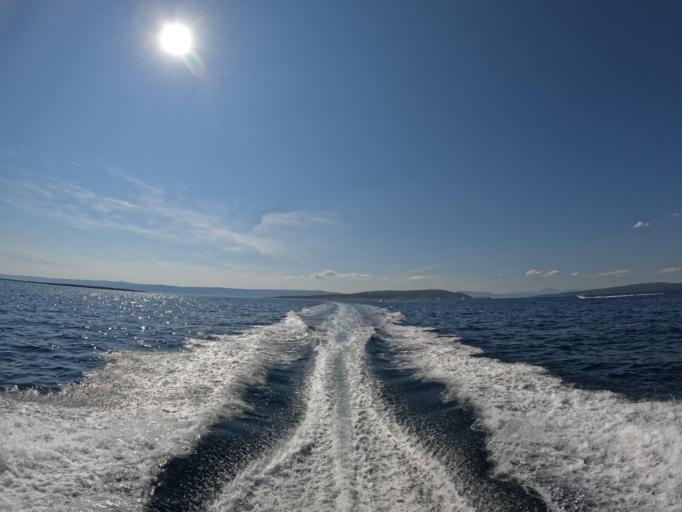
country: HR
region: Primorsko-Goranska
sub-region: Grad Krk
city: Krk
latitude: 44.9541
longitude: 14.5819
